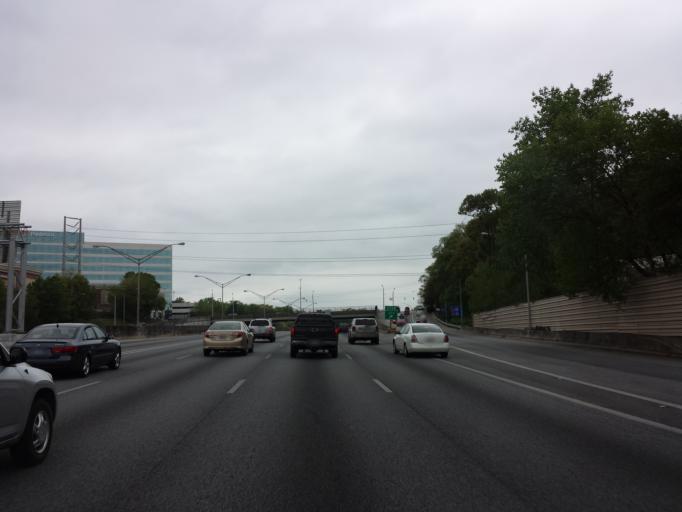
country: US
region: Georgia
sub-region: Fulton County
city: Atlanta
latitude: 33.8043
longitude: -84.4107
